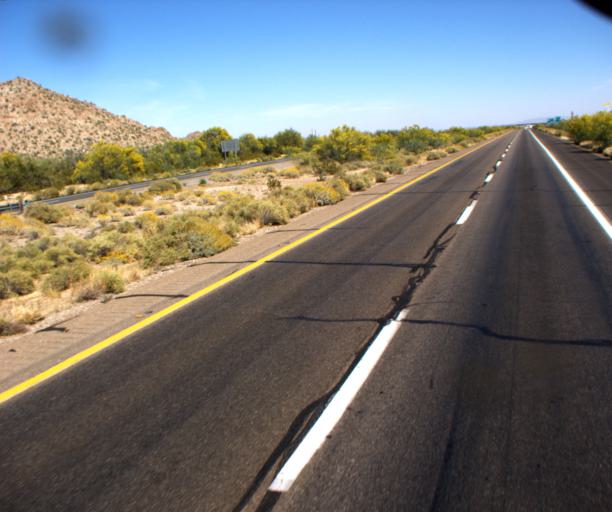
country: US
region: Arizona
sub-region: Pinal County
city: Maricopa
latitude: 32.8347
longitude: -112.1430
